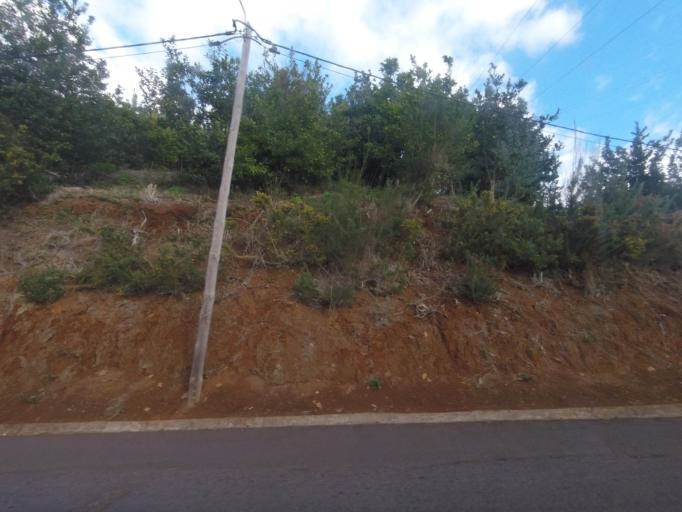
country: PT
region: Madeira
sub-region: Santa Cruz
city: Camacha
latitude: 32.6633
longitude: -16.8689
